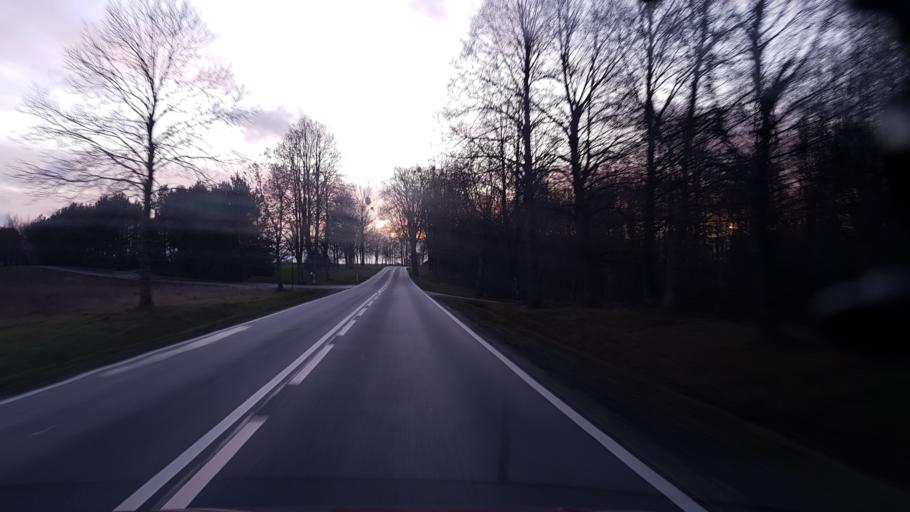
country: PL
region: Pomeranian Voivodeship
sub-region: Powiat bytowski
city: Tuchomie
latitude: 54.1293
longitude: 17.3856
